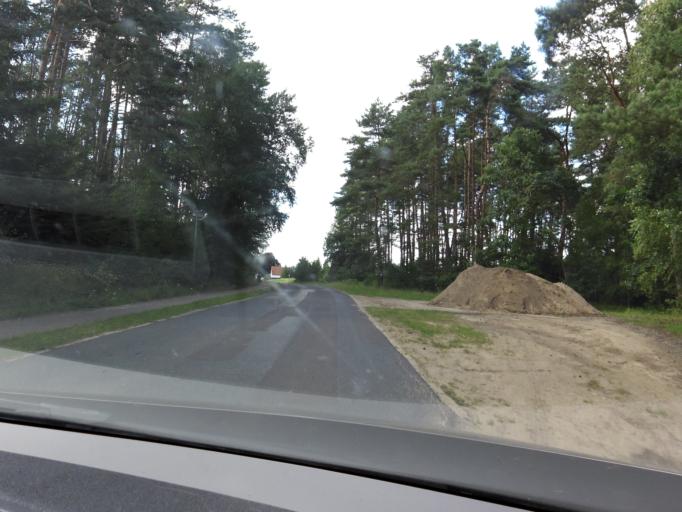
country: DE
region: Brandenburg
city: Lychen
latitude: 53.2250
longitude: 13.2752
